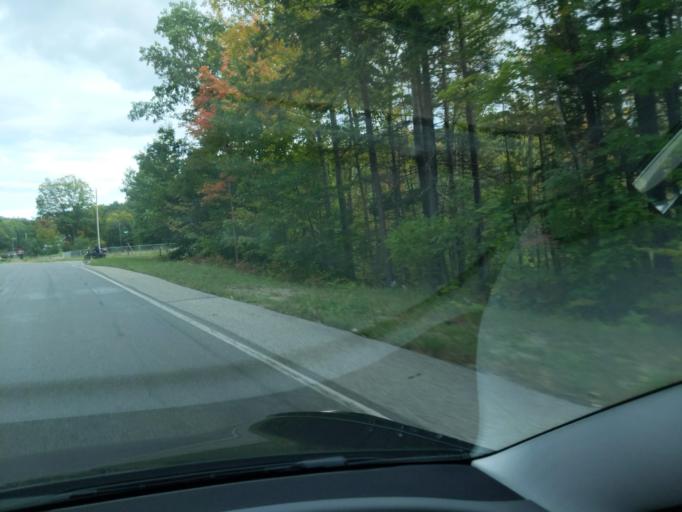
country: US
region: Michigan
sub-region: Kalkaska County
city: Rapid City
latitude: 44.7818
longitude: -85.2739
